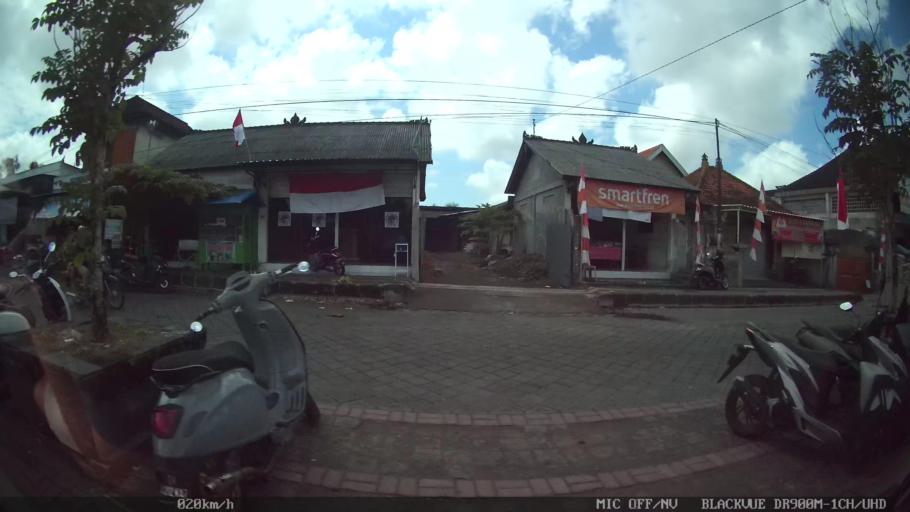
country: ID
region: Bali
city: Banjar Sedang
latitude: -8.5676
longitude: 115.2944
